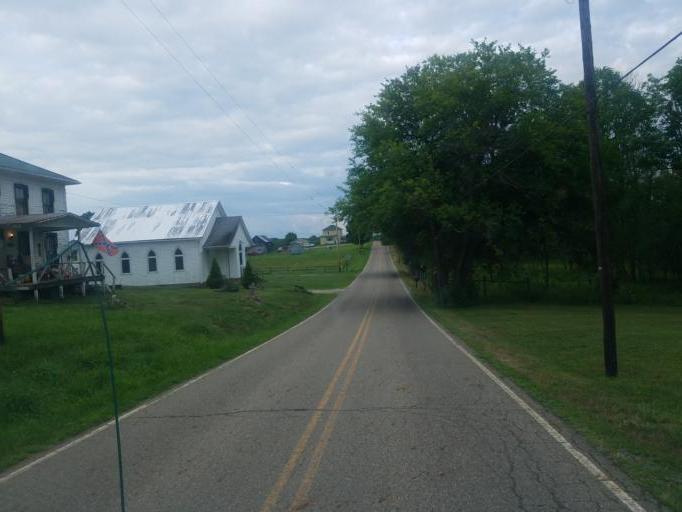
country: US
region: Ohio
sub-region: Knox County
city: Oak Hill
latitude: 40.4181
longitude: -82.1367
